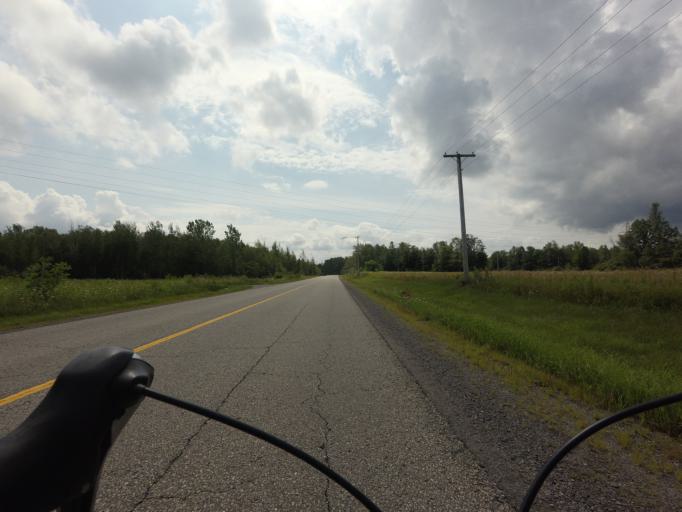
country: CA
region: Ontario
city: Brockville
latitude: 44.6386
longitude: -75.6717
